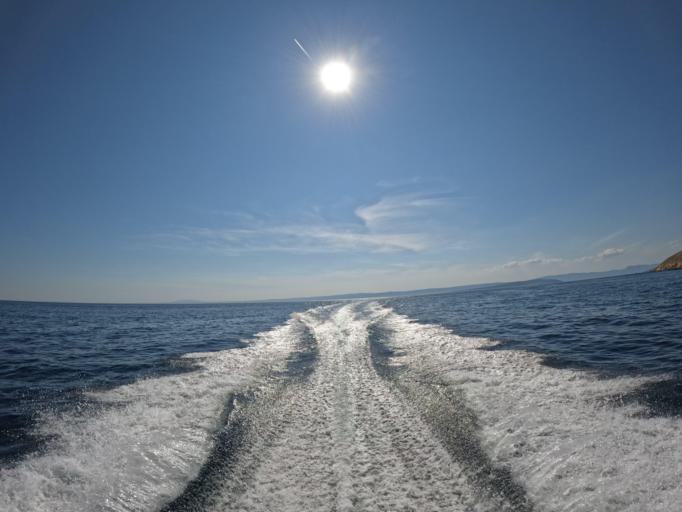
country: HR
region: Primorsko-Goranska
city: Punat
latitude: 44.9622
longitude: 14.6550
